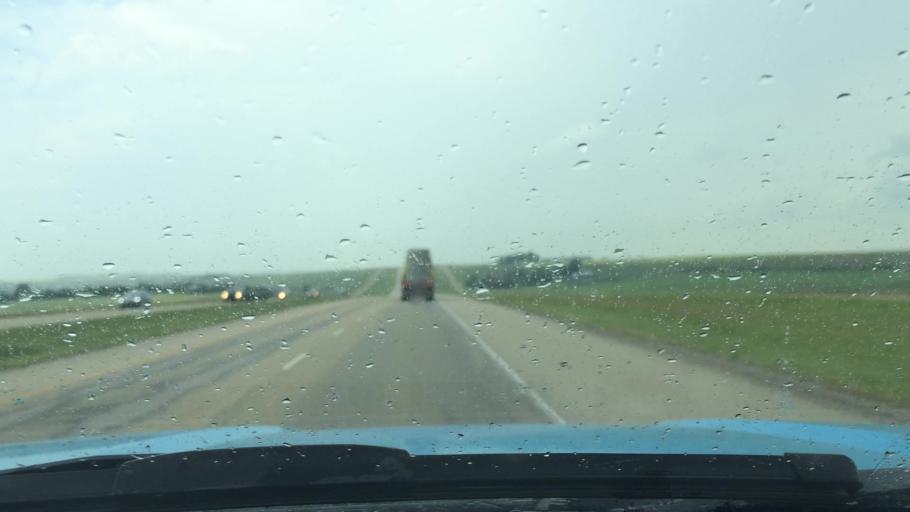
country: CA
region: Alberta
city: Carstairs
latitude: 51.5414
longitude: -114.0250
